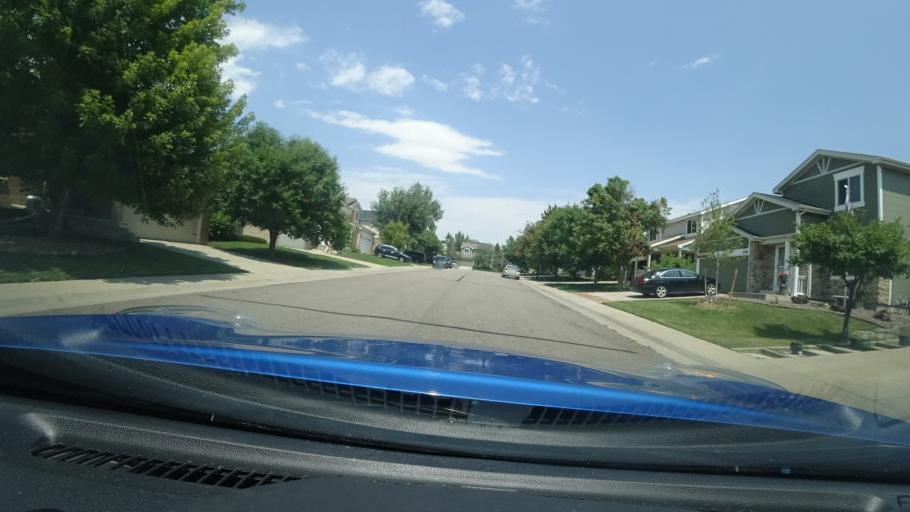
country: US
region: Colorado
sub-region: Adams County
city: Aurora
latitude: 39.6710
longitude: -104.7572
